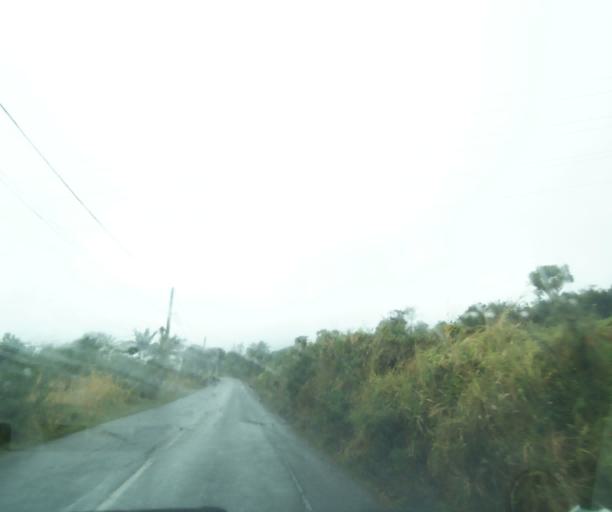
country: RE
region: Reunion
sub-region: Reunion
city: Saint-Paul
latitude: -21.0151
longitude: 55.3071
